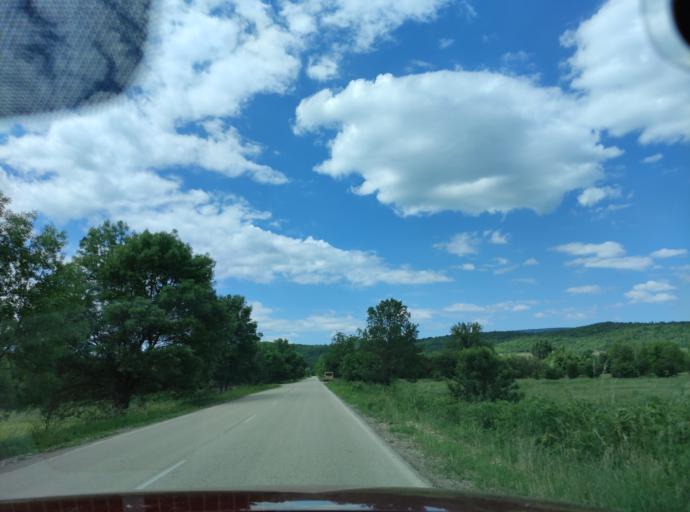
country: BG
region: Montana
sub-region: Obshtina Montana
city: Montana
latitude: 43.3964
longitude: 23.0732
